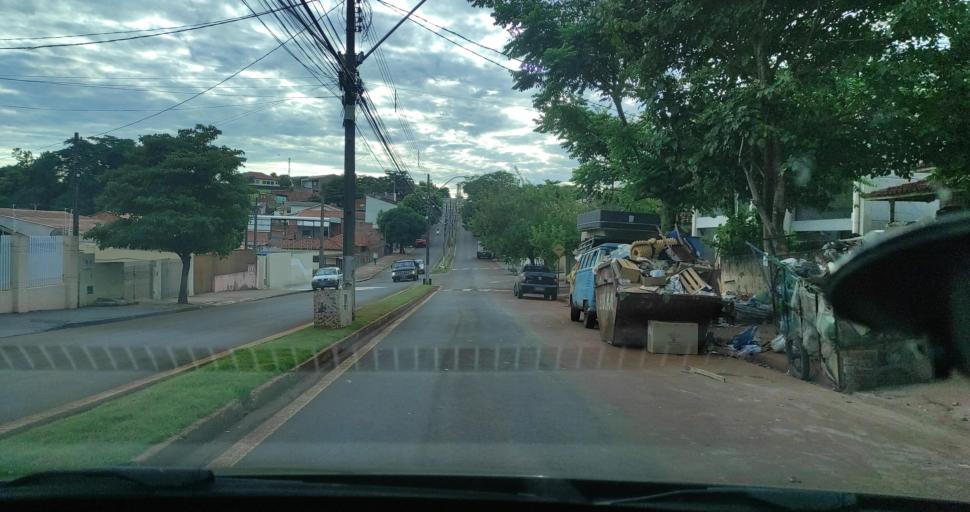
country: BR
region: Parana
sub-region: Ibipora
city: Ibipora
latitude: -23.2667
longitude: -51.0426
